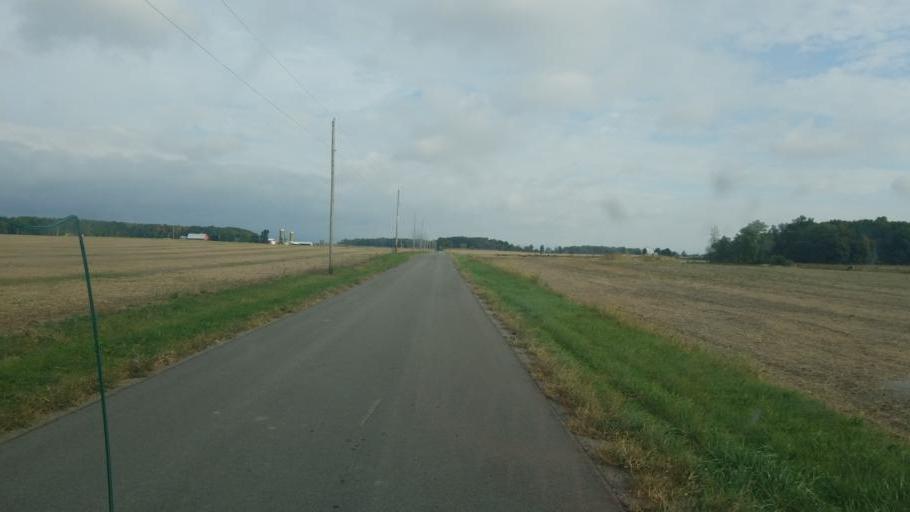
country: US
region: Ohio
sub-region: Wyandot County
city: Carey
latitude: 41.0243
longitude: -83.4487
